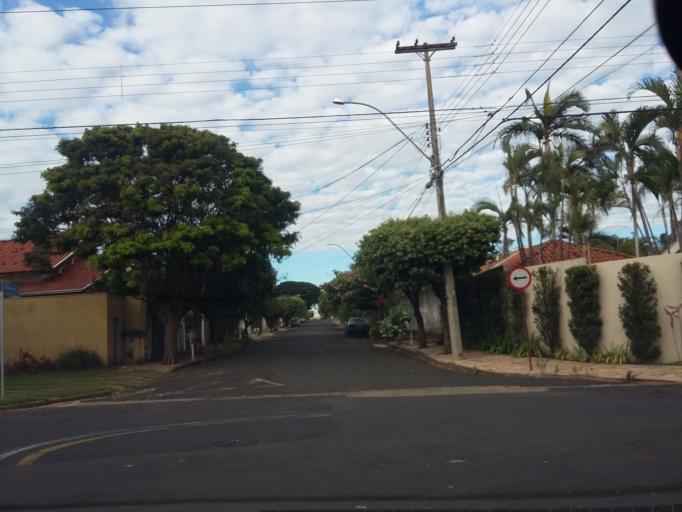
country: BR
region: Sao Paulo
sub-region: Sao Jose Do Rio Preto
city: Sao Jose do Rio Preto
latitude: -20.8402
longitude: -49.4041
